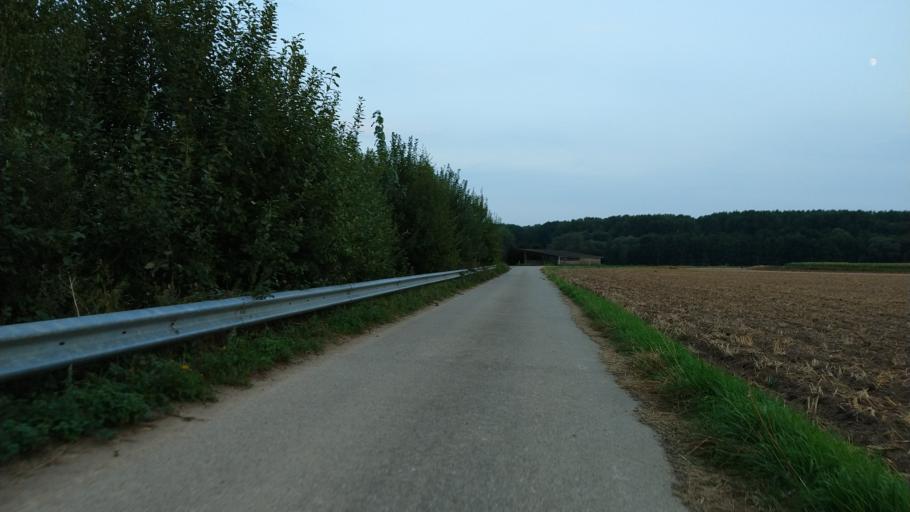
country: BE
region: Flanders
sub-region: Provincie Vlaams-Brabant
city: Boutersem
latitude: 50.8401
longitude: 4.8159
